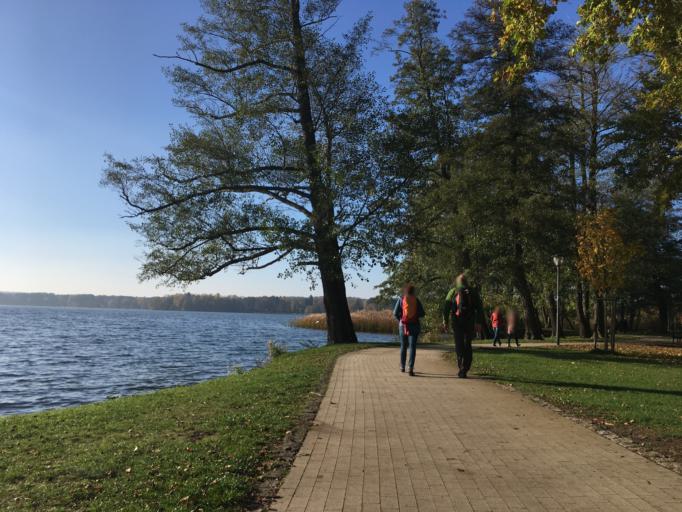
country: DE
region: Brandenburg
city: Bad Saarow
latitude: 52.2907
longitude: 14.0556
